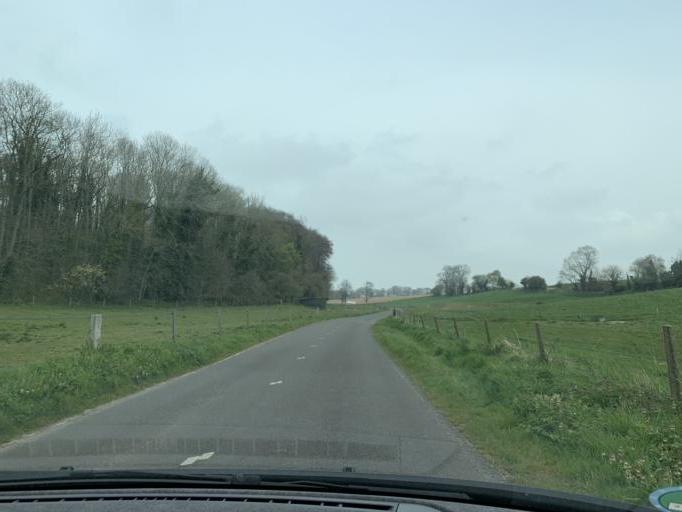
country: FR
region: Haute-Normandie
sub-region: Departement de la Seine-Maritime
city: Saint-Valery-en-Caux
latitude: 49.8527
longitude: 0.7379
